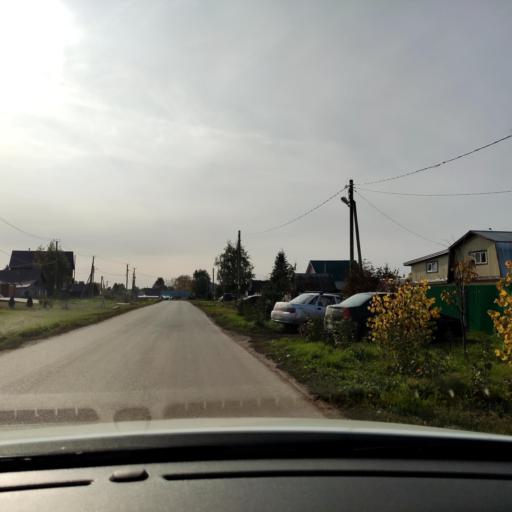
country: RU
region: Tatarstan
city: Vysokaya Gora
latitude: 55.8747
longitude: 49.3794
